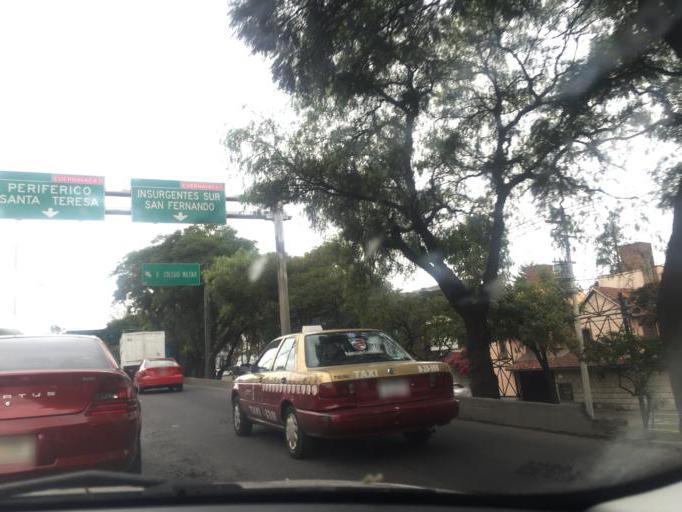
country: MX
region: Mexico City
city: Tlalpan
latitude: 19.2792
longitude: -99.1641
